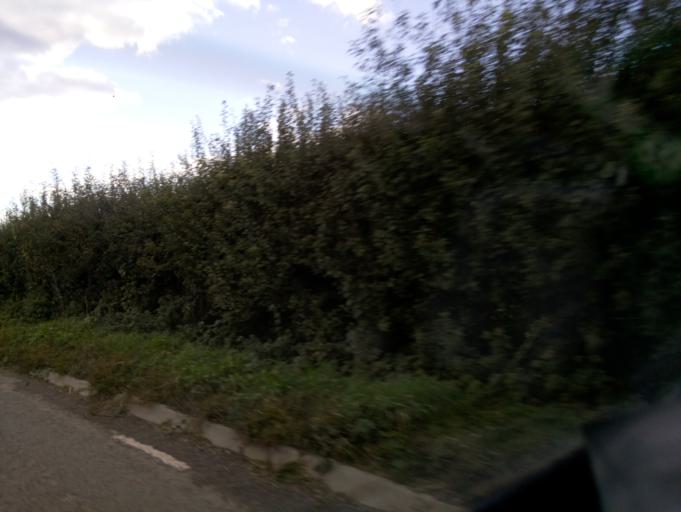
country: GB
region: England
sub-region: Herefordshire
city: Withington
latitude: 52.0596
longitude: -2.6140
